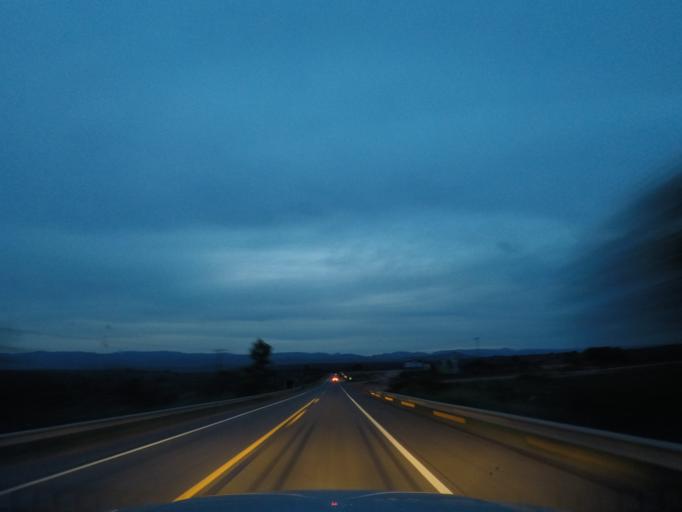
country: BR
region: Bahia
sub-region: Andarai
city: Vera Cruz
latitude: -12.4968
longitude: -41.2981
